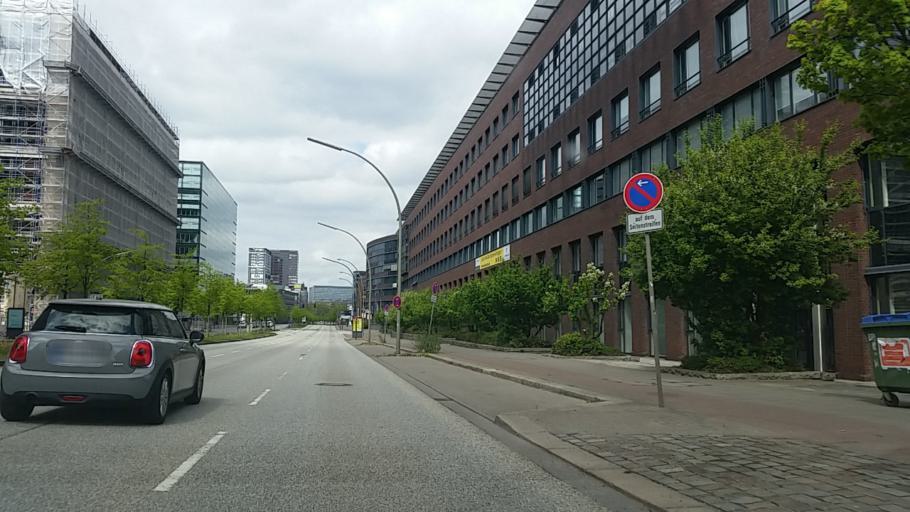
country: DE
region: Hamburg
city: Hammerbrook
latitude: 53.5464
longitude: 10.0300
